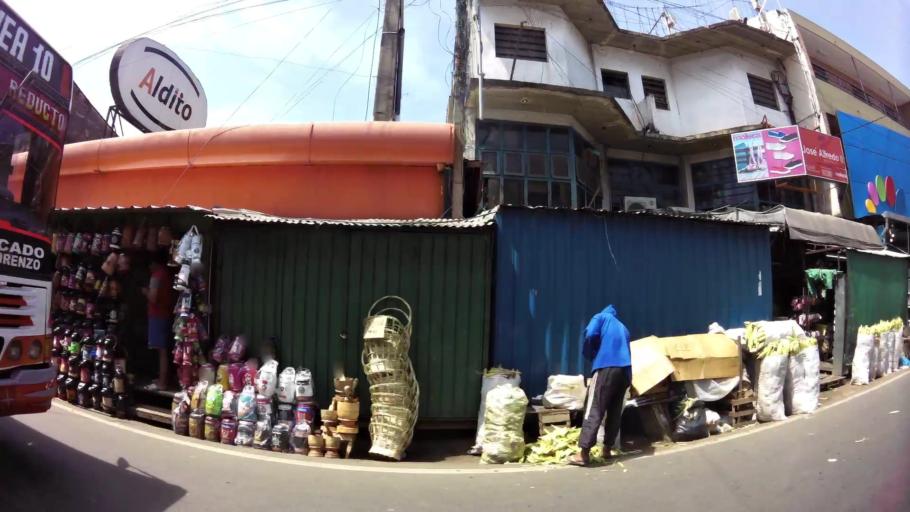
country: PY
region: Central
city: San Lorenzo
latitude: -25.3448
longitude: -57.5102
